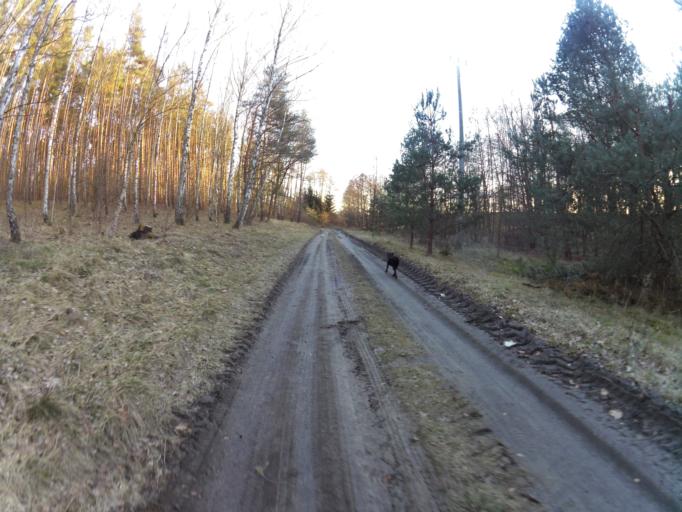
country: PL
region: West Pomeranian Voivodeship
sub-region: Powiat mysliborski
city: Debno
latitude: 52.8269
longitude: 14.7795
